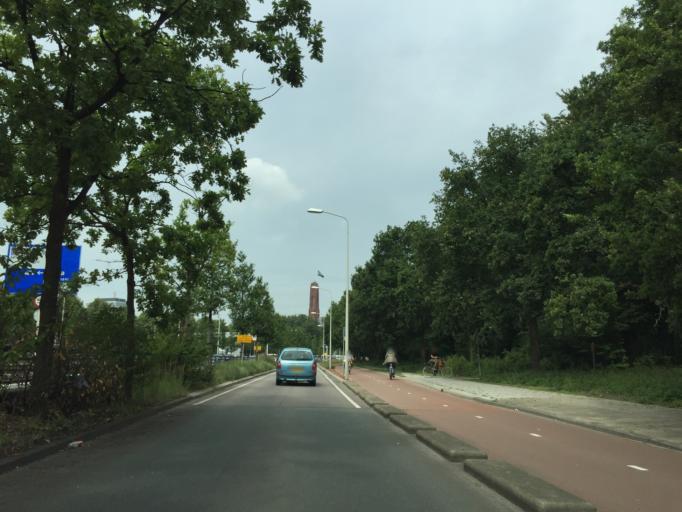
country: NL
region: South Holland
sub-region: Gemeente Den Haag
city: The Hague
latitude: 52.0855
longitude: 4.3247
